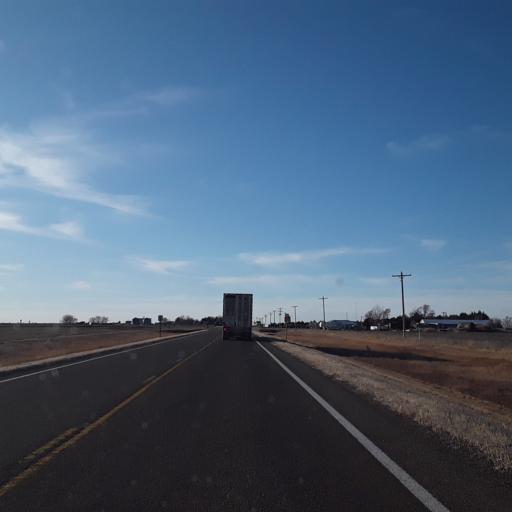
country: US
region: Kansas
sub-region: Cheyenne County
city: Saint Francis
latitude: 39.7566
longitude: -101.7064
